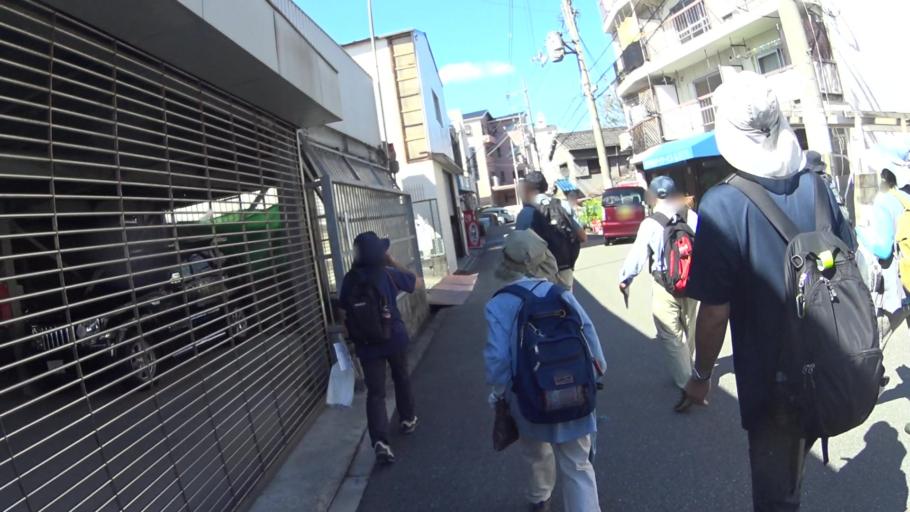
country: JP
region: Osaka
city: Yao
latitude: 34.6339
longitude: 135.5526
